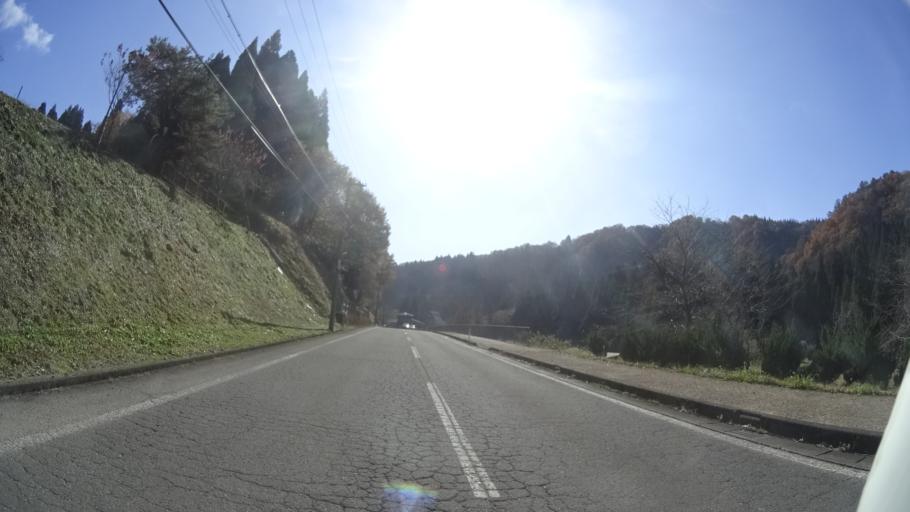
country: JP
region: Fukui
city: Ono
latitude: 35.8640
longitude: 136.3627
